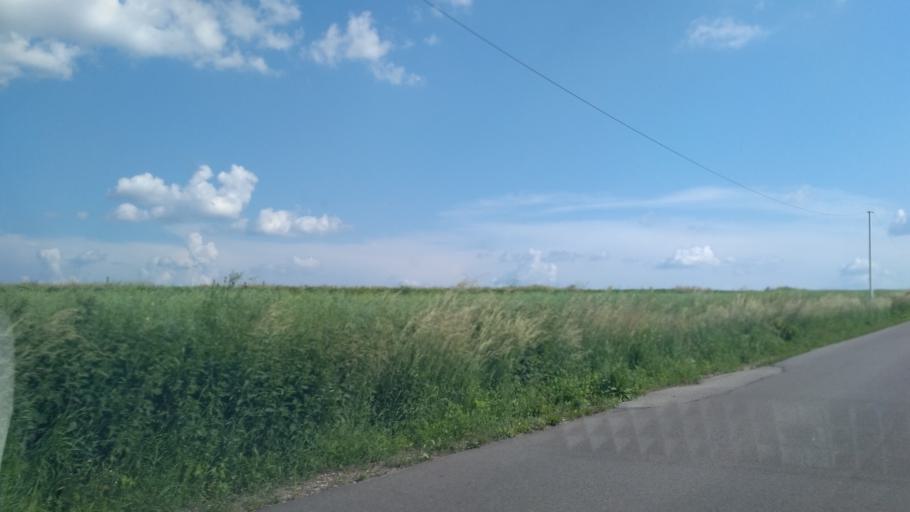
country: PL
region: Subcarpathian Voivodeship
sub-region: Powiat jaroslawski
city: Ostrow
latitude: 49.9353
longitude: 22.7399
